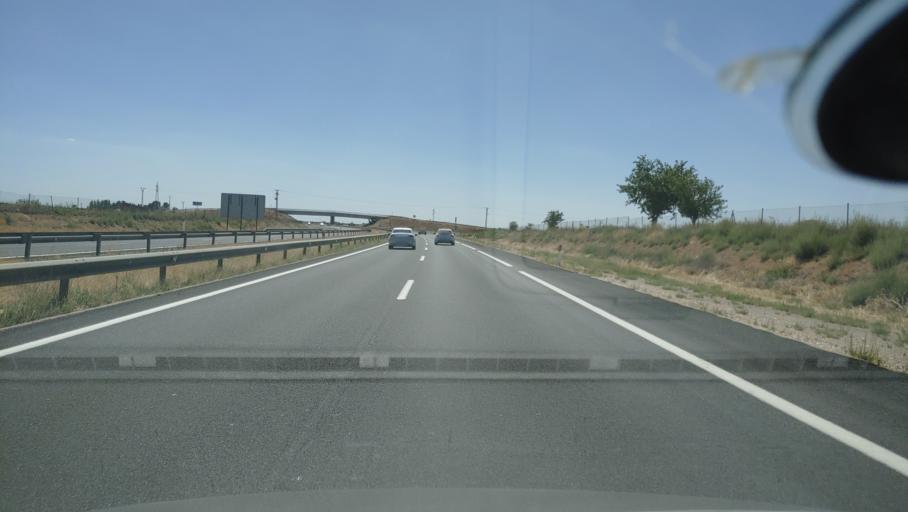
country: ES
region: Castille-La Mancha
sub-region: Provincia de Ciudad Real
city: Villarta de San Juan
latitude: 39.2248
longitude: -3.4125
